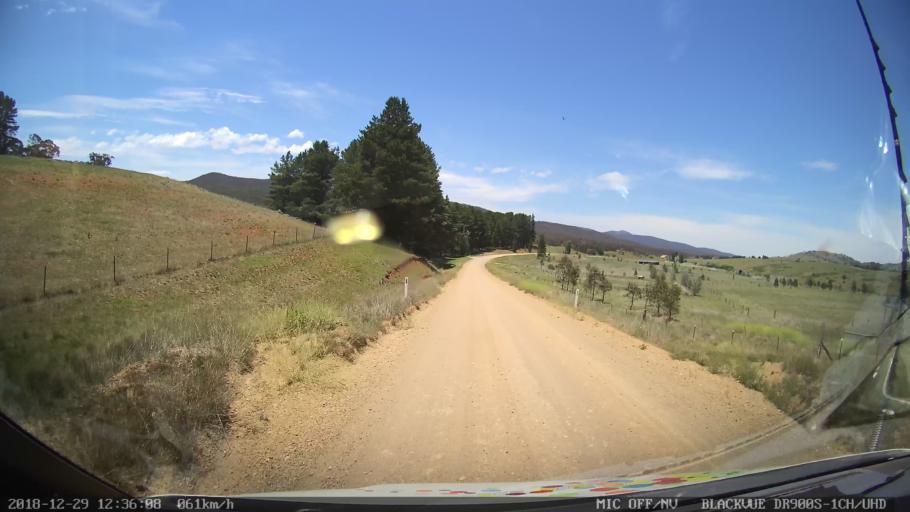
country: AU
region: Australian Capital Territory
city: Macarthur
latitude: -35.5679
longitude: 149.2252
